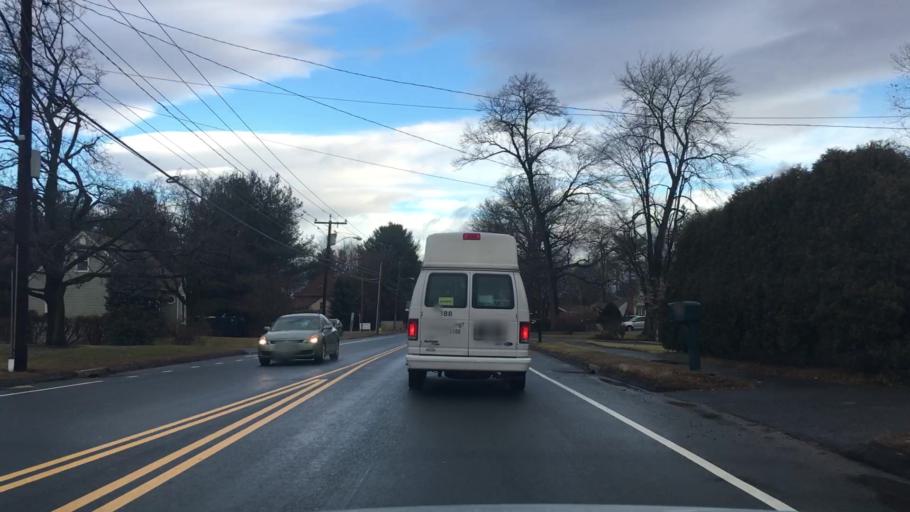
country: US
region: Massachusetts
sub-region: Hampden County
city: Agawam
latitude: 42.0680
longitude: -72.6314
